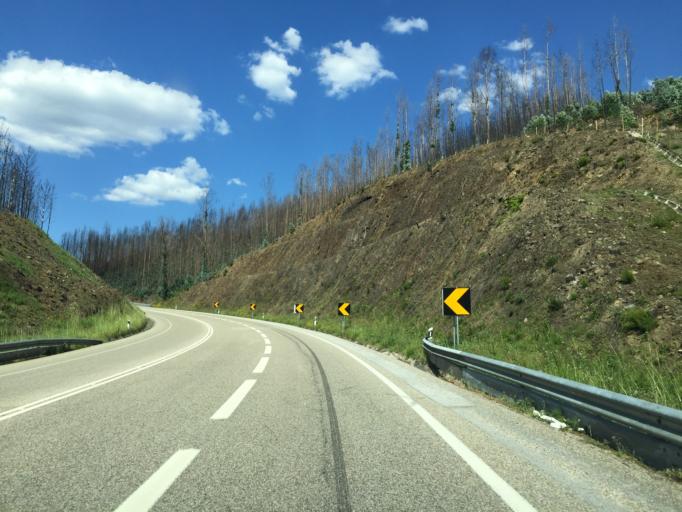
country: PT
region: Leiria
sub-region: Figueiro Dos Vinhos
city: Figueiro dos Vinhos
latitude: 39.9267
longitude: -8.3024
